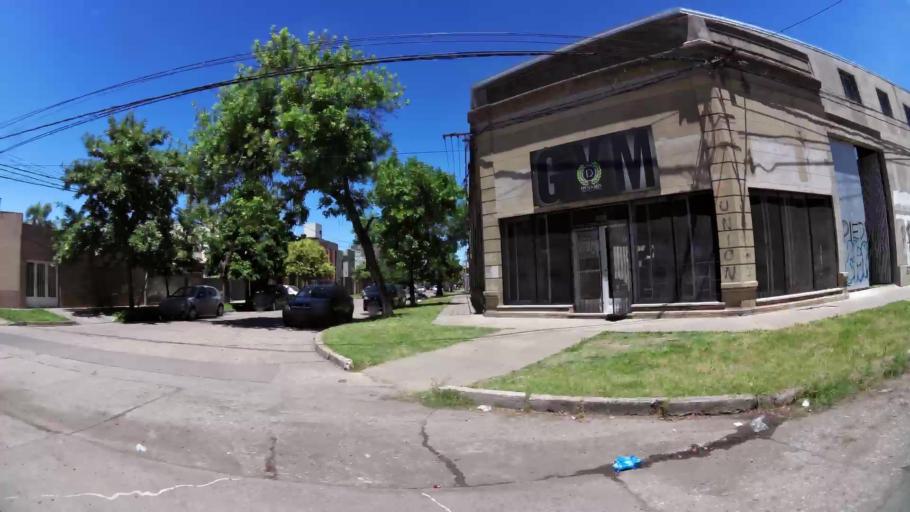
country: AR
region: Santa Fe
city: Santa Fe de la Vera Cruz
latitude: -31.6503
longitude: -60.7213
